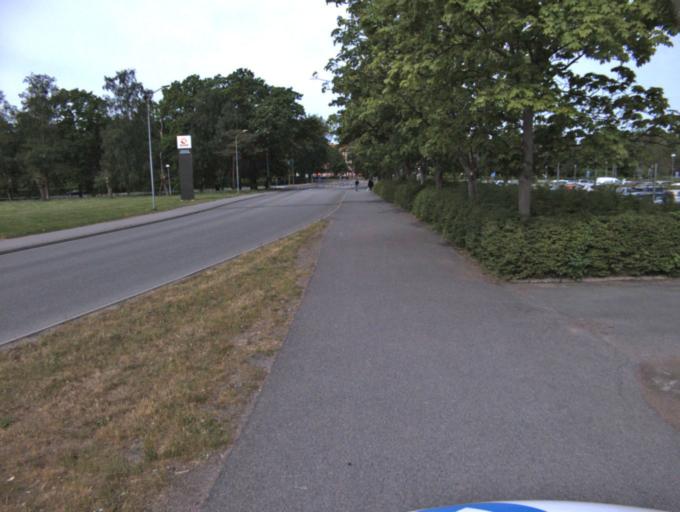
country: SE
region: Skane
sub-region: Kristianstads Kommun
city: Kristianstad
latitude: 56.0307
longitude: 14.1706
